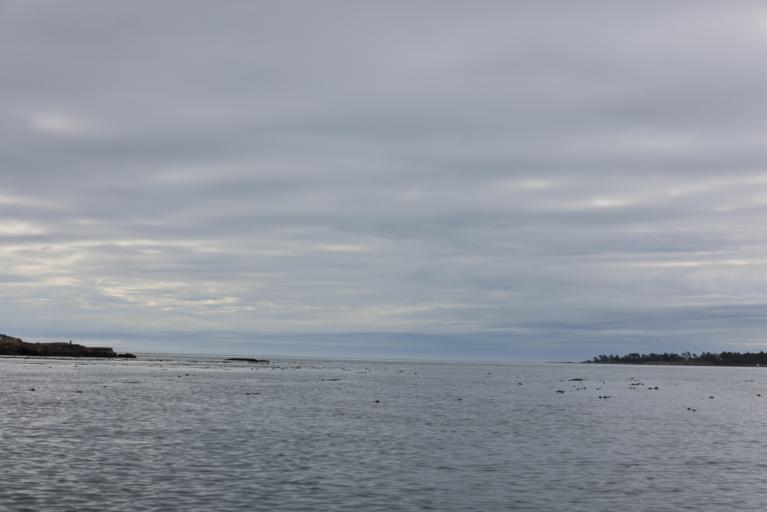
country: CA
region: British Columbia
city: Oak Bay
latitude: 48.4496
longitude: -123.2741
